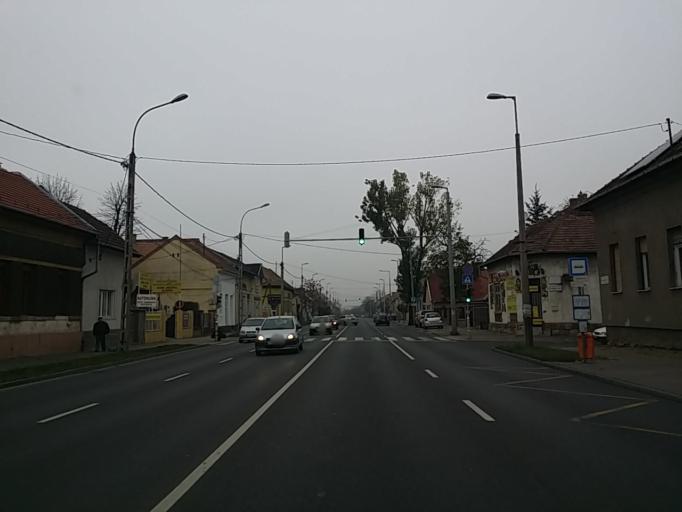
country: HU
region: Budapest
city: Budapest XV. keruelet
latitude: 47.5572
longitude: 19.1258
